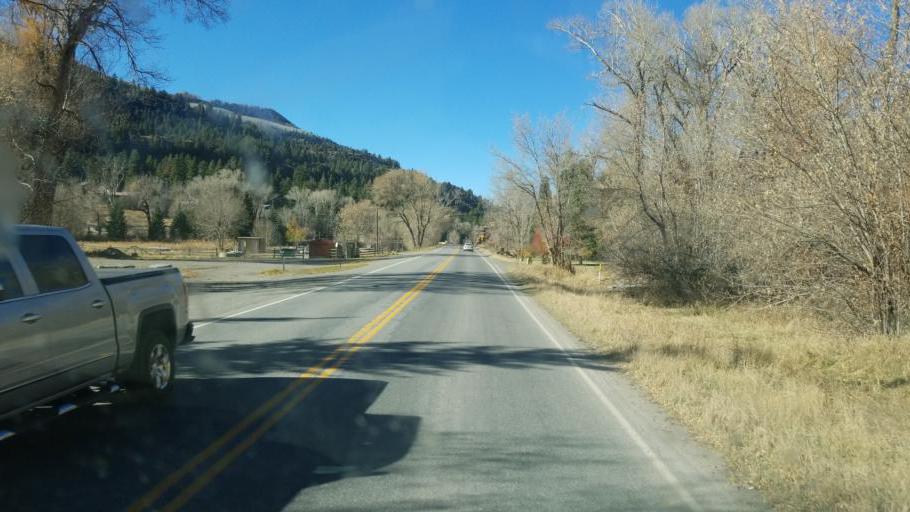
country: US
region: Colorado
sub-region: Ouray County
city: Ouray
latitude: 38.0509
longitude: -107.6848
